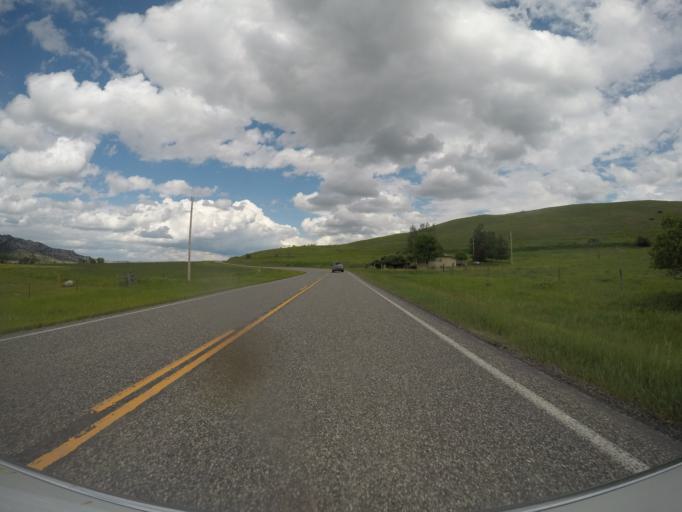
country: US
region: Montana
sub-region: Sweet Grass County
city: Big Timber
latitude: 45.6899
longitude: -110.0499
